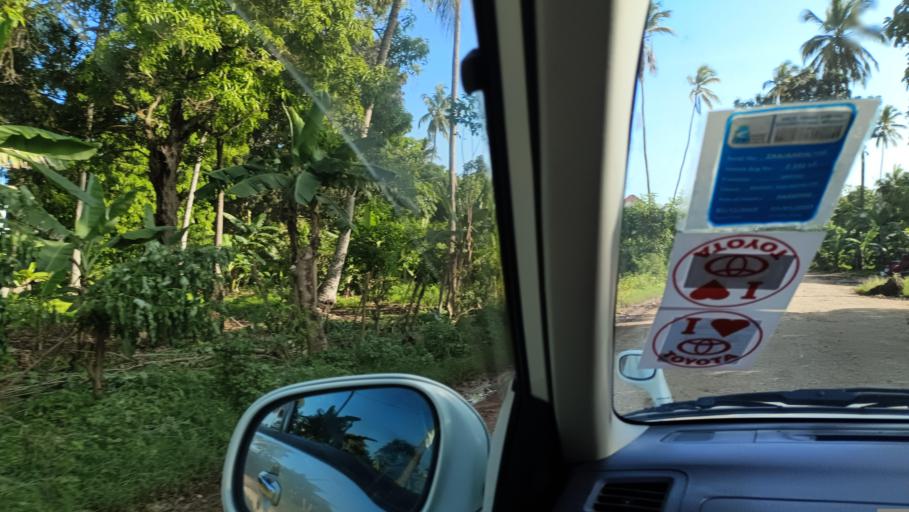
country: TZ
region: Zanzibar Urban/West
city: Zanzibar
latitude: -6.2335
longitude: 39.2194
